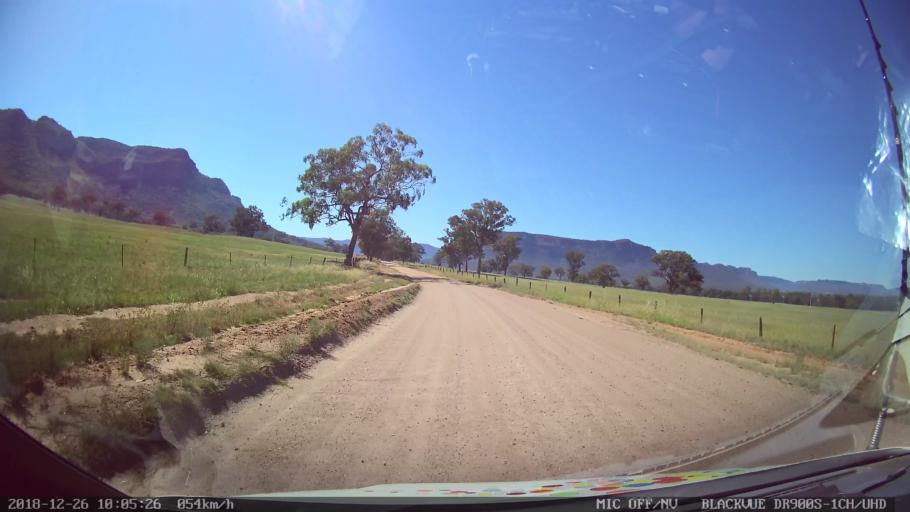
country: AU
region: New South Wales
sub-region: Mid-Western Regional
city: Kandos
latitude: -33.0778
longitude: 150.2119
